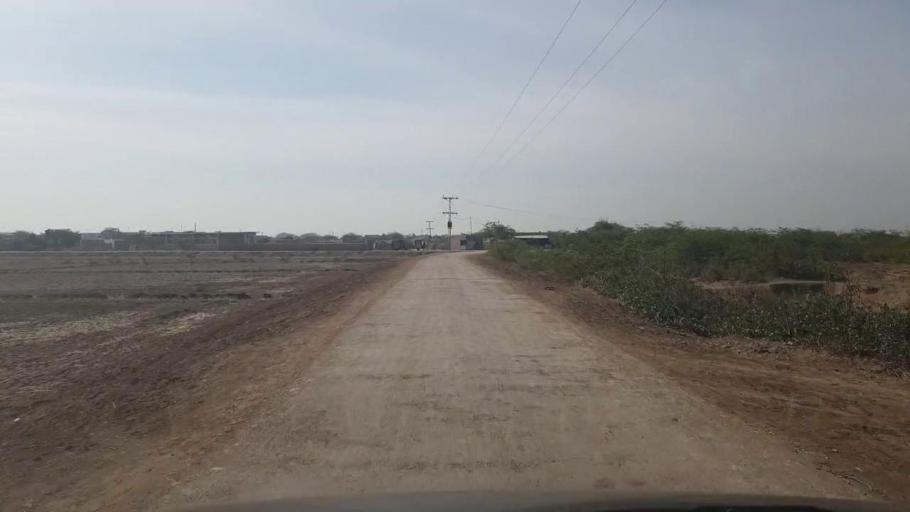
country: PK
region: Sindh
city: Umarkot
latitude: 25.3532
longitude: 69.6785
